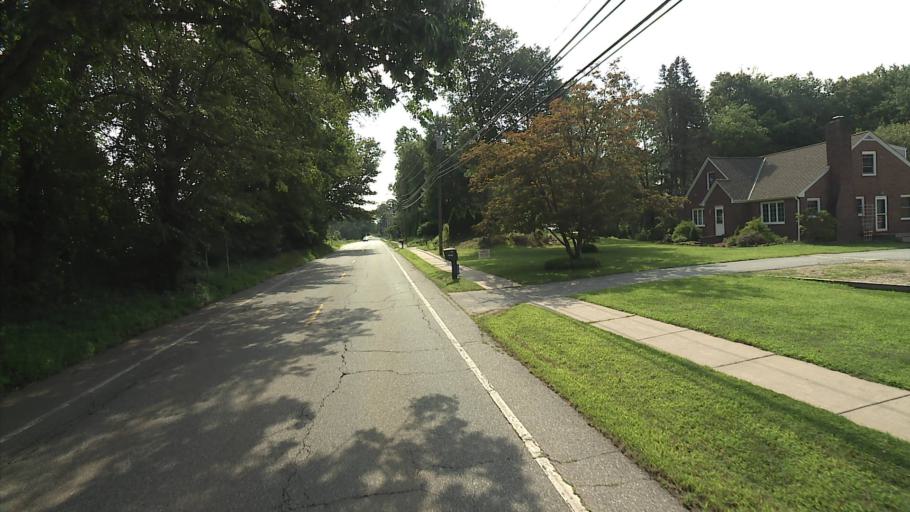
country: US
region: Connecticut
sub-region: New London County
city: Colchester
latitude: 41.5743
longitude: -72.3130
